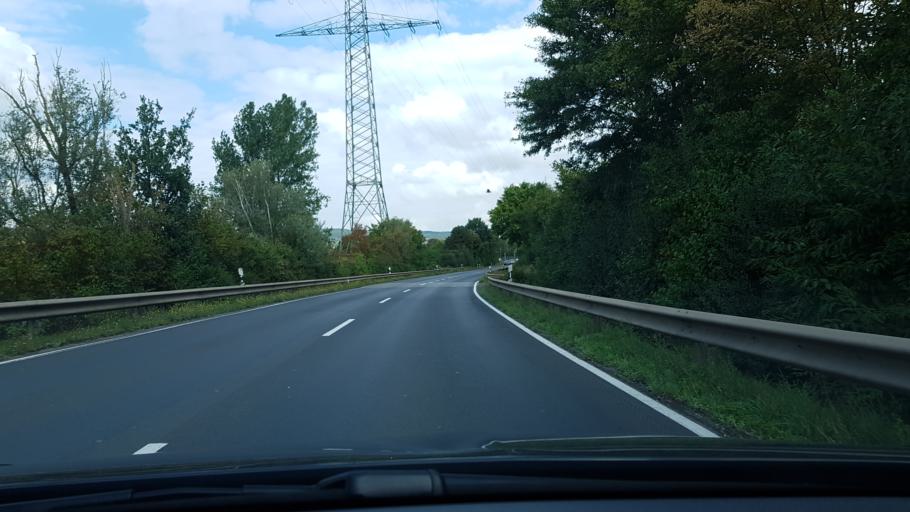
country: DE
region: Rheinland-Pfalz
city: Andernach
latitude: 50.4320
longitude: 7.4225
